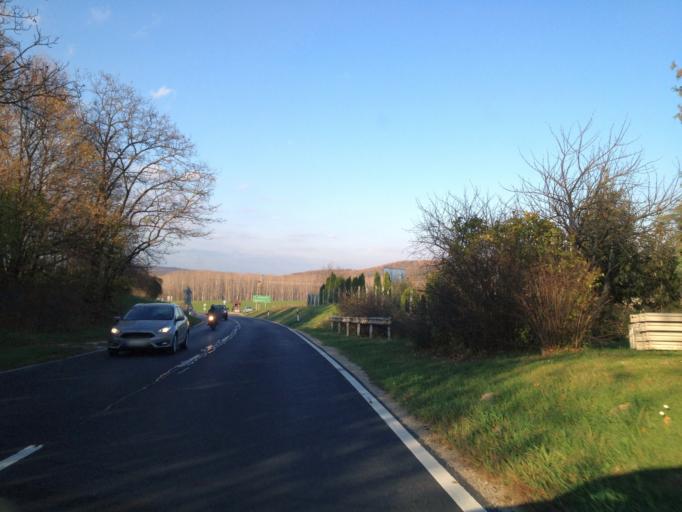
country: HU
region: Gyor-Moson-Sopron
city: Bakonyszentlaszlo
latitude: 47.3640
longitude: 17.8748
